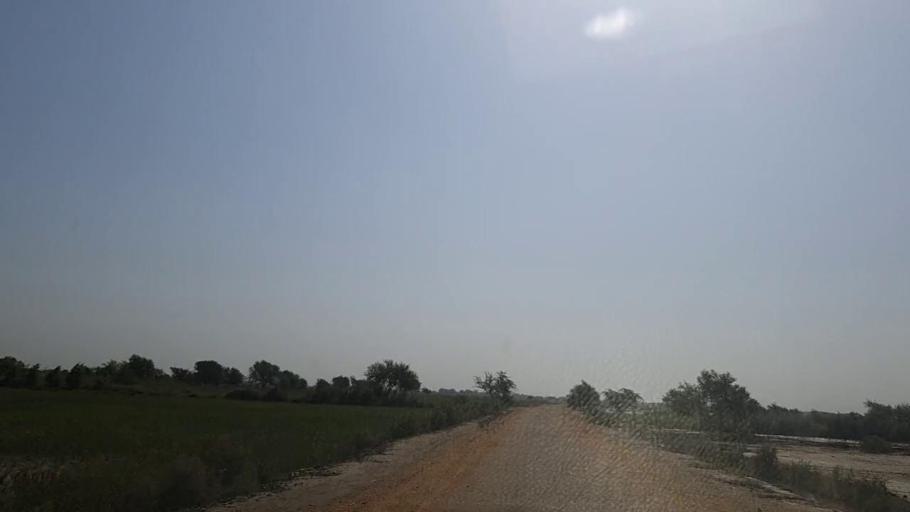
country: PK
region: Sindh
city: Daro Mehar
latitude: 24.7073
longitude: 68.1257
